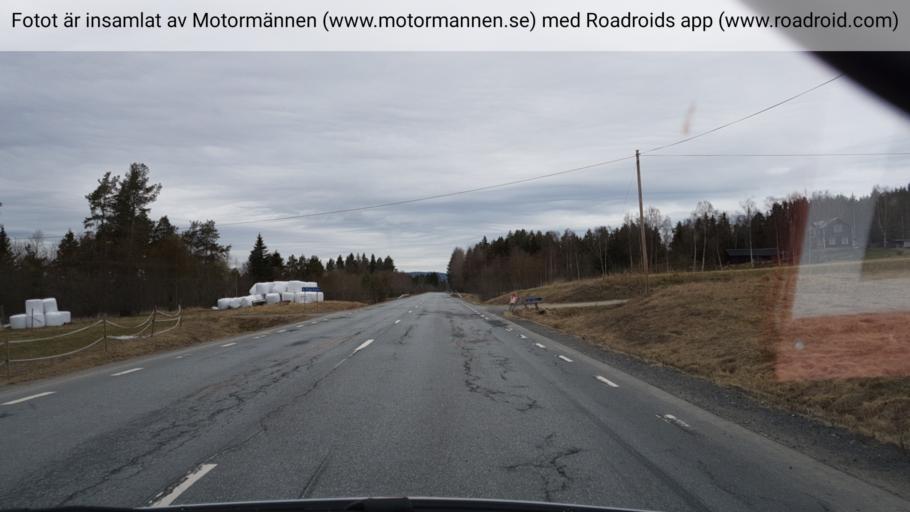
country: SE
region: Vaesternorrland
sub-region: Solleftea Kommun
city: Solleftea
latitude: 63.2152
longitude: 17.2260
